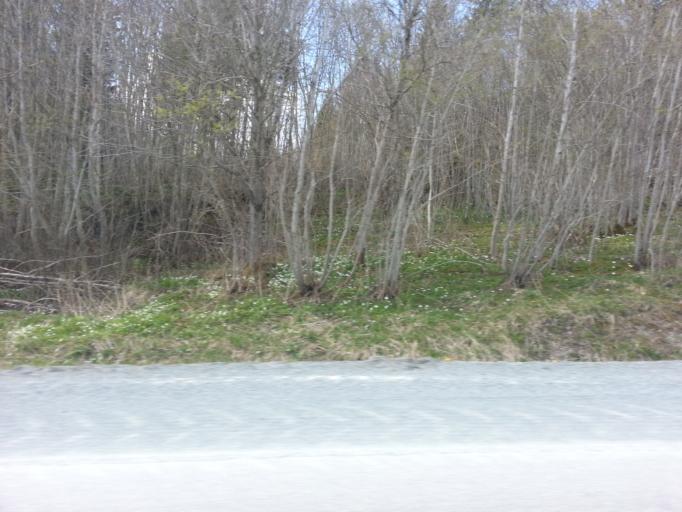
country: NO
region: Nord-Trondelag
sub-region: Levanger
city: Skogn
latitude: 63.6412
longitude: 11.2487
